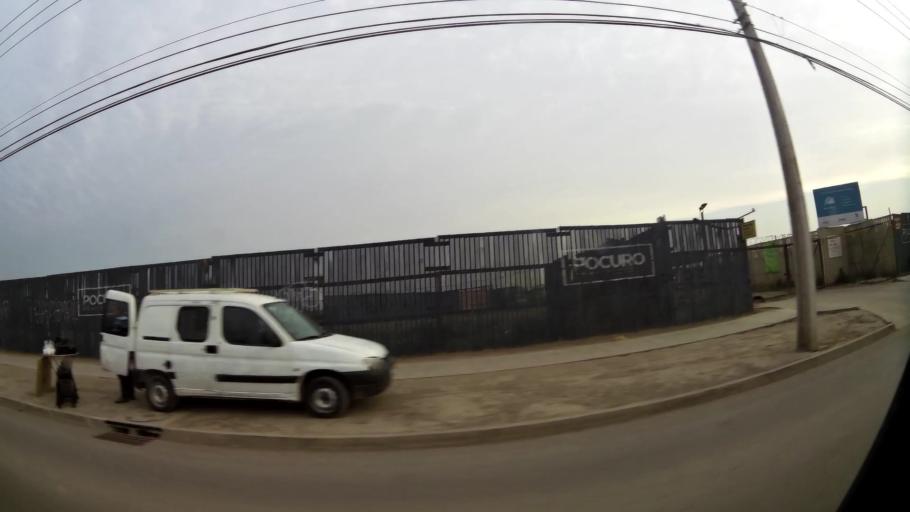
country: CL
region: Santiago Metropolitan
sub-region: Provincia de Talagante
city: Penaflor
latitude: -33.5318
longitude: -70.7947
